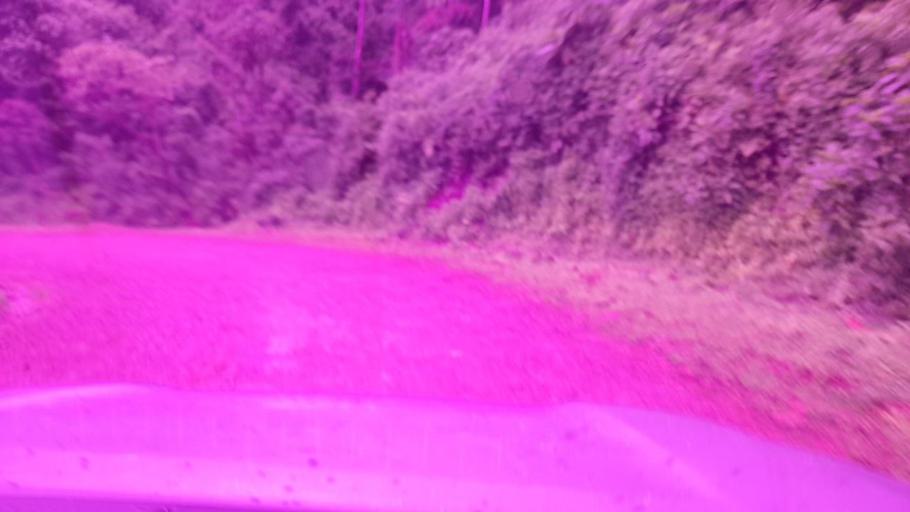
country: ET
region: Southern Nations, Nationalities, and People's Region
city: Bonga
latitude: 7.5085
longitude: 36.0654
